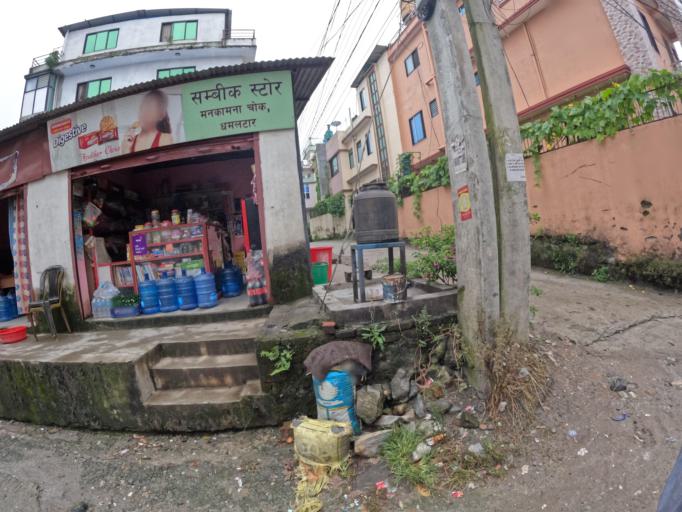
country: NP
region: Central Region
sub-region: Bagmati Zone
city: Kathmandu
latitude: 27.7574
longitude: 85.3194
